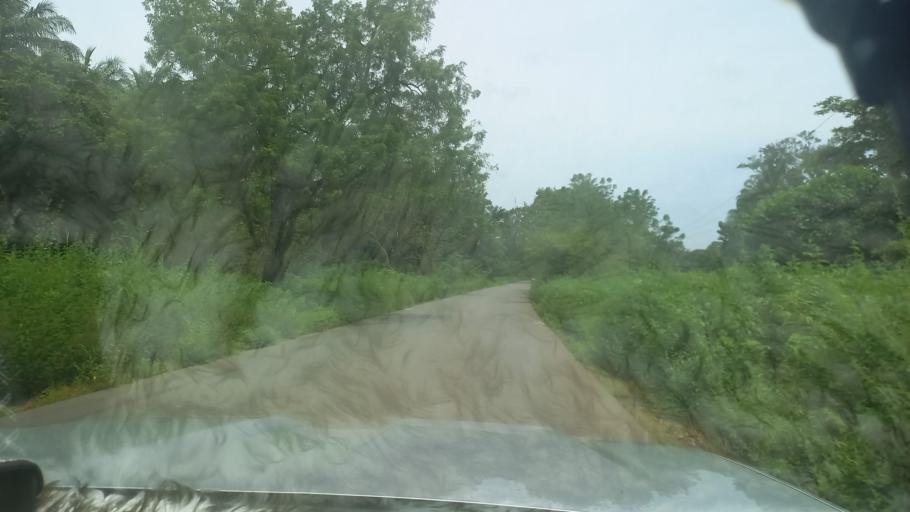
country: SN
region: Kolda
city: Marsassoum
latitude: 12.9557
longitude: -16.0050
